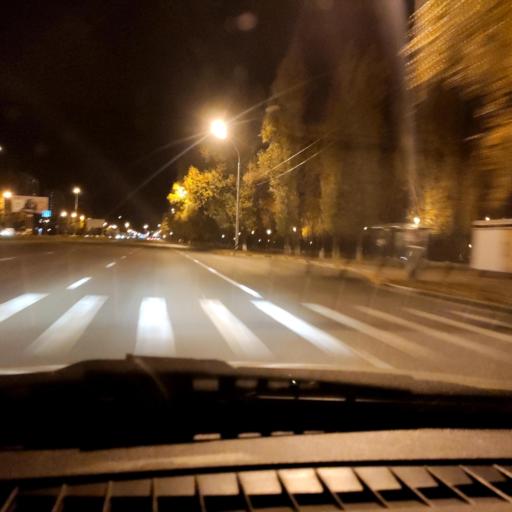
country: RU
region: Samara
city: Tol'yatti
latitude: 53.5118
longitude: 49.2771
